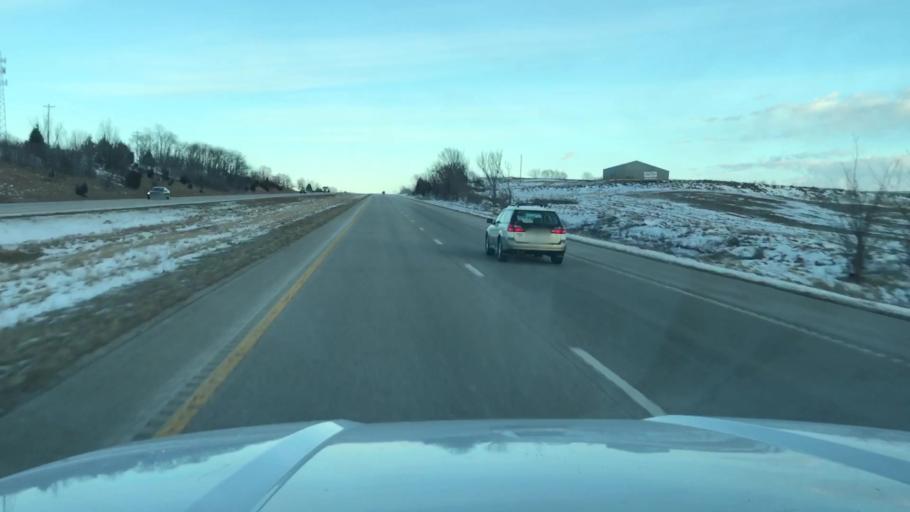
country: US
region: Missouri
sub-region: Clinton County
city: Gower
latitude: 39.7473
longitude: -94.6543
